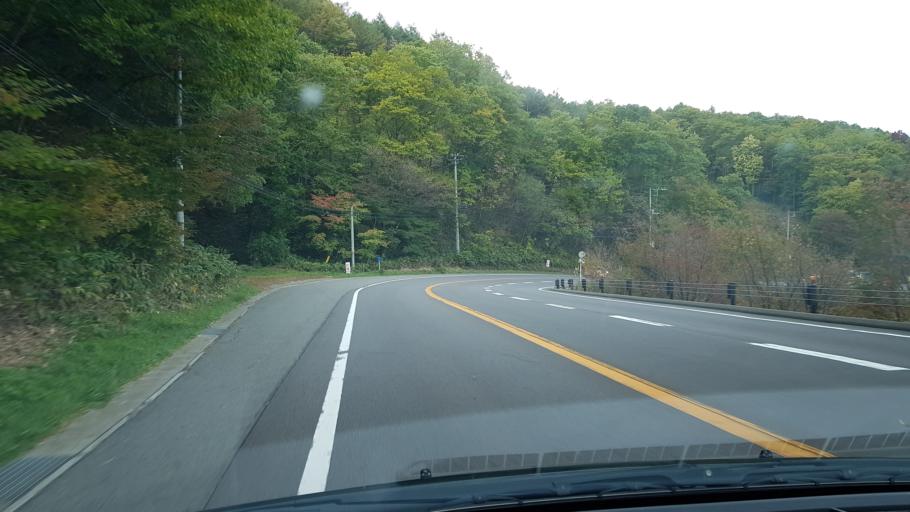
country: JP
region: Gunma
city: Nakanojomachi
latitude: 36.5986
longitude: 138.5868
